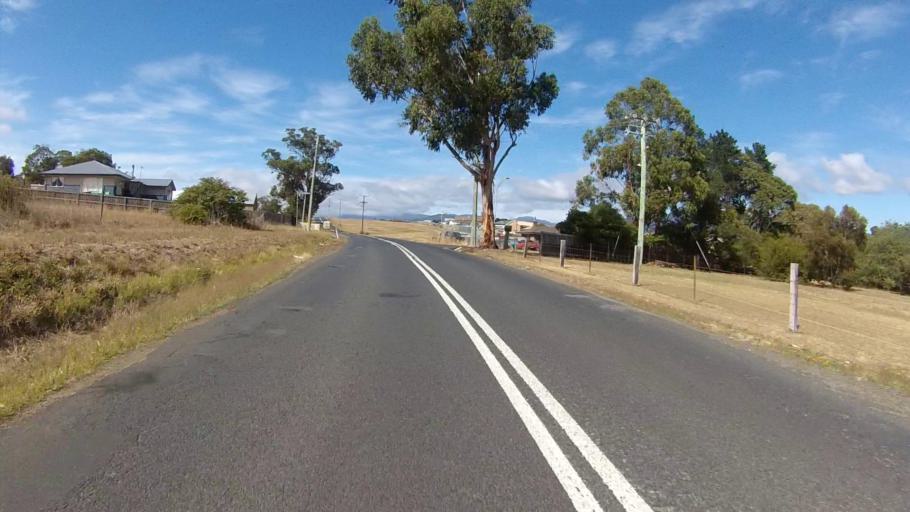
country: AU
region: Tasmania
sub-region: Brighton
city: Old Beach
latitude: -42.7458
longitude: 147.2814
